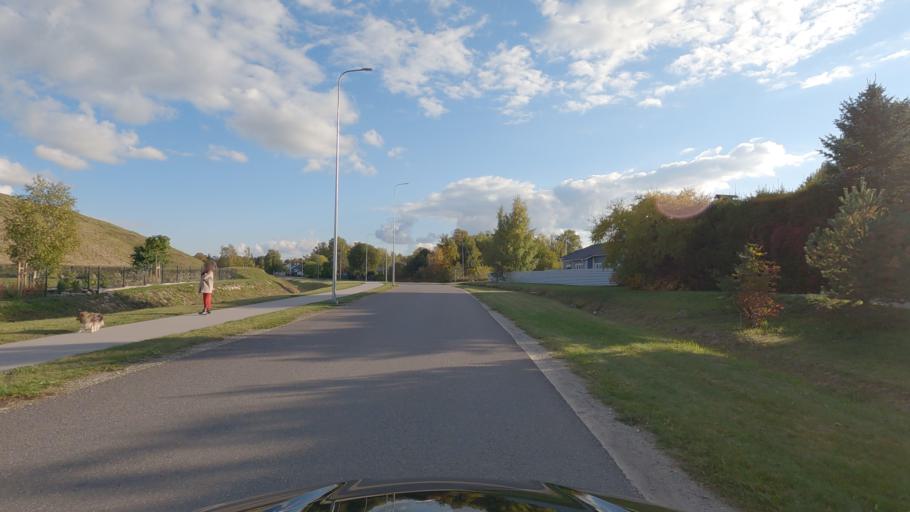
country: EE
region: Harju
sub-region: Saku vald
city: Saku
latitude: 59.3041
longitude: 24.6500
